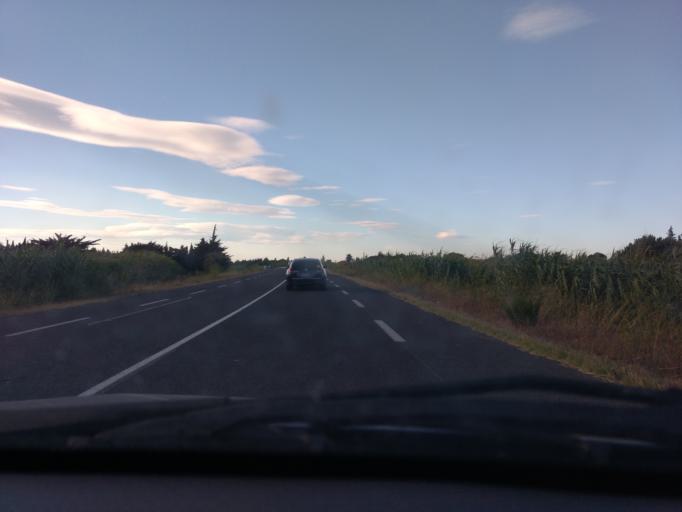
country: FR
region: Languedoc-Roussillon
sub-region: Departement des Pyrenees-Orientales
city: Sainte-Marie-Plage
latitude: 42.7216
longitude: 3.0298
